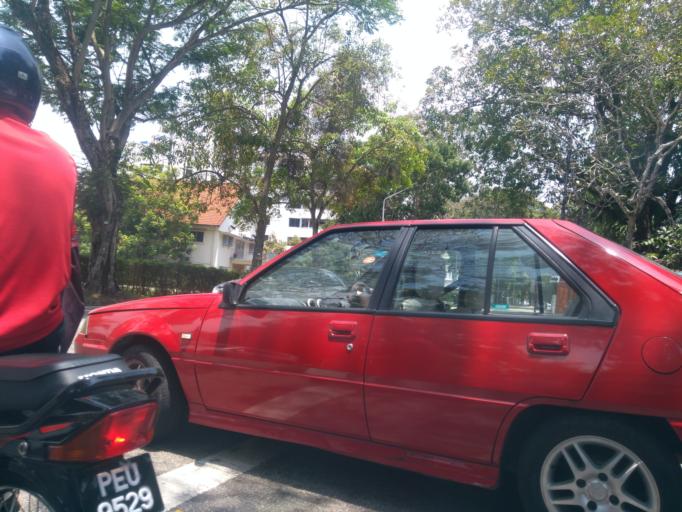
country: MY
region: Penang
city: George Town
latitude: 5.4263
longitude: 100.3095
